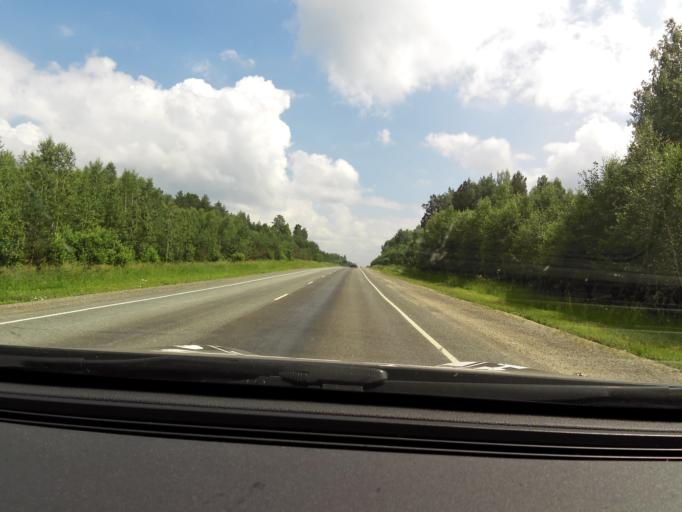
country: RU
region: Sverdlovsk
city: Achit
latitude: 56.8501
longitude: 57.7284
